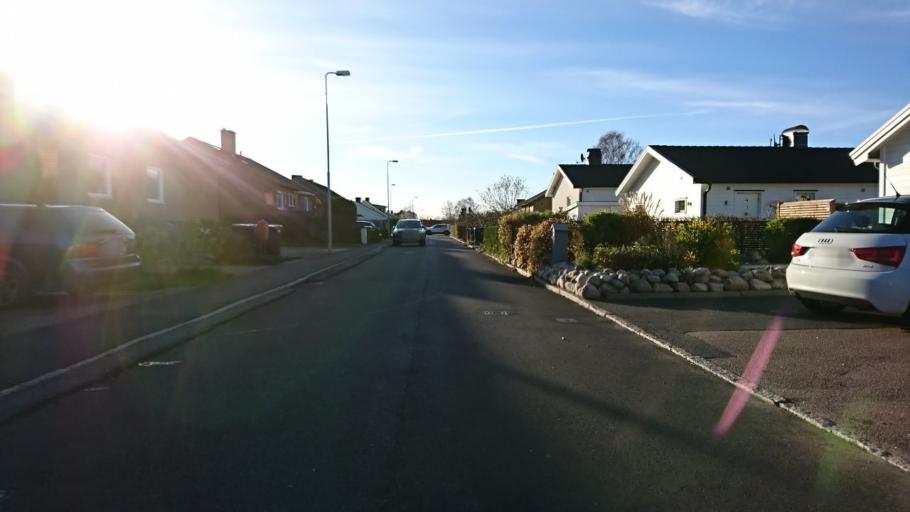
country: SE
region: Vaestra Goetaland
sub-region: Molndal
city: Moelndal
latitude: 57.6520
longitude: 11.9937
